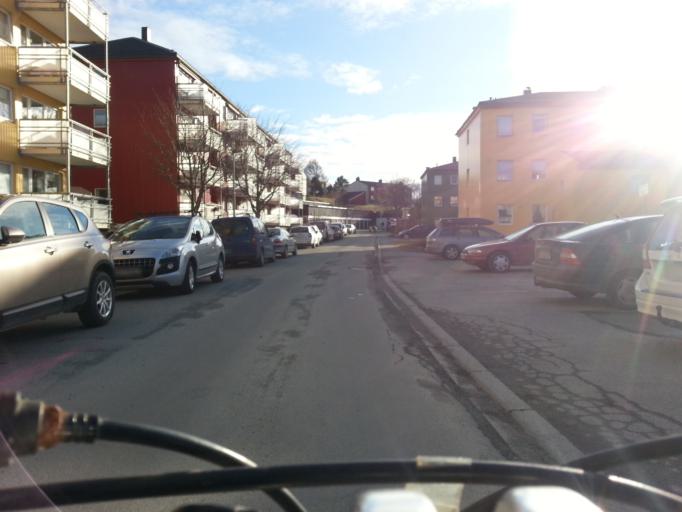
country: NO
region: Sor-Trondelag
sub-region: Trondheim
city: Trondheim
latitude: 63.4530
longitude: 10.4448
